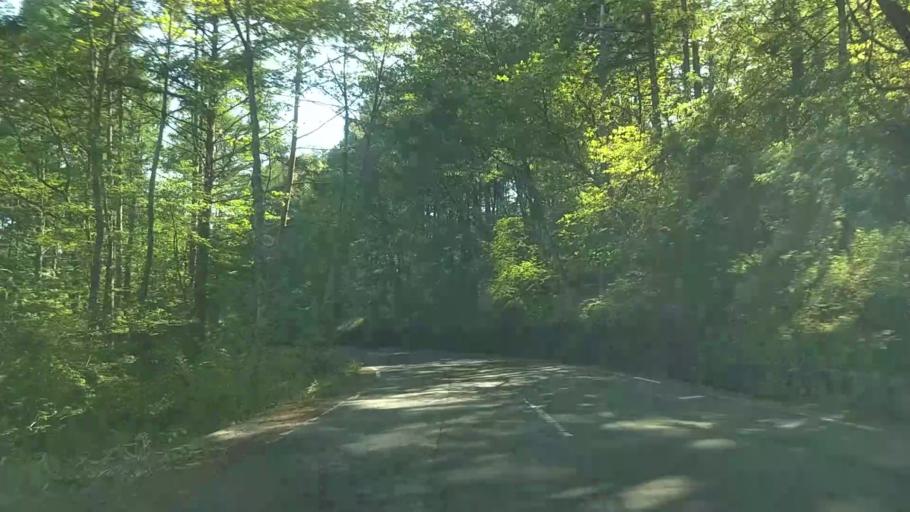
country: JP
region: Yamanashi
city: Nirasaki
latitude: 35.8951
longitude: 138.4054
